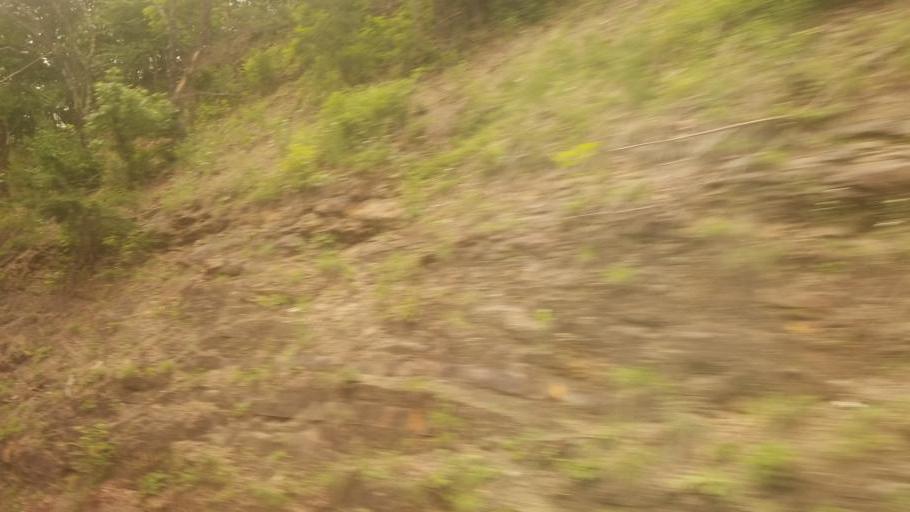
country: US
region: West Virginia
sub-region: Morgan County
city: Berkeley Springs
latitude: 39.5976
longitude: -78.3989
